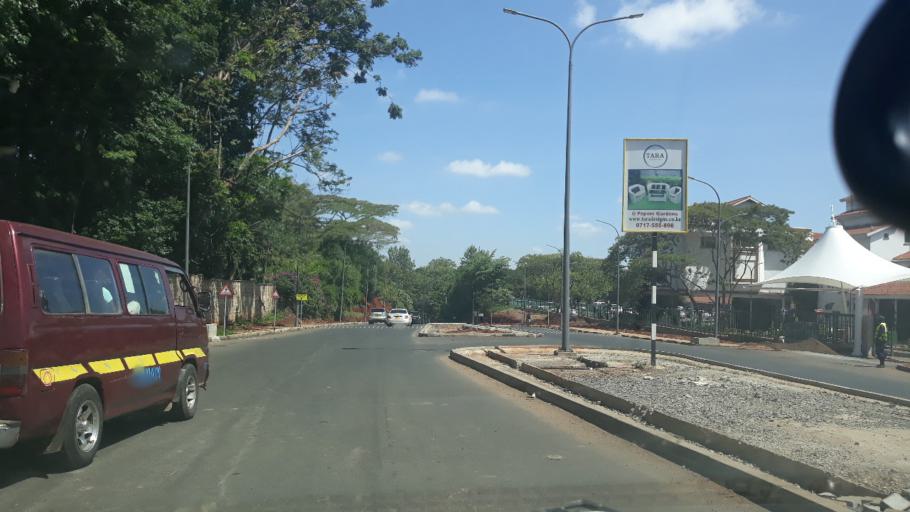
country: KE
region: Nairobi Area
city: Nairobi
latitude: -1.2290
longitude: 36.8043
